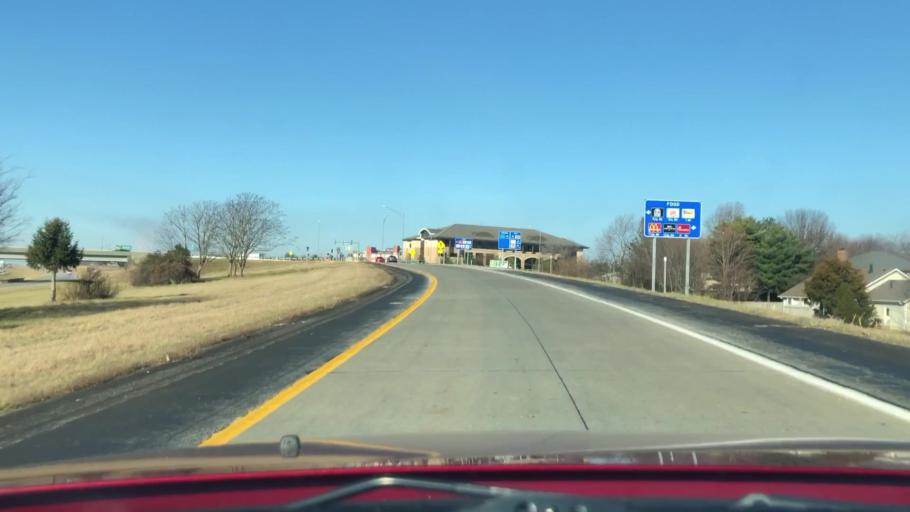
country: US
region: Missouri
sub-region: Greene County
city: Battlefield
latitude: 37.1426
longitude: -93.3168
